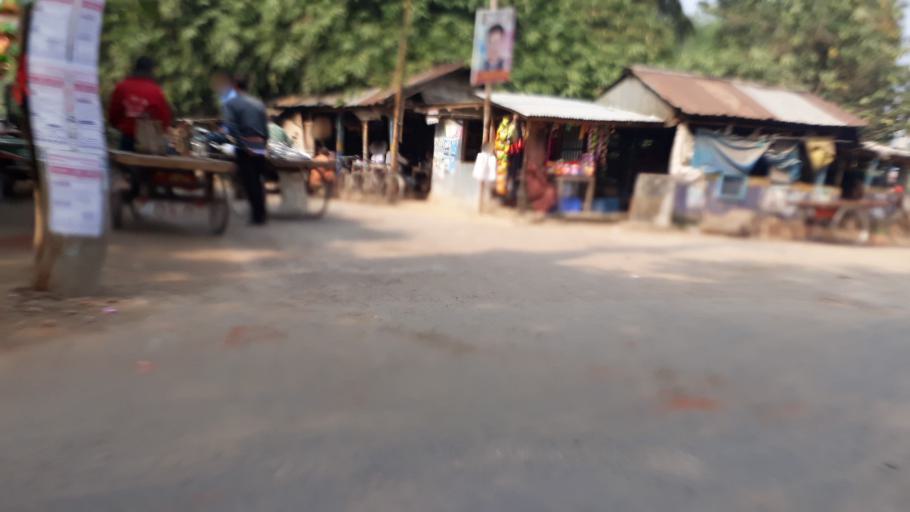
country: BD
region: Khulna
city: Kaliganj
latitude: 23.3510
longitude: 88.8998
